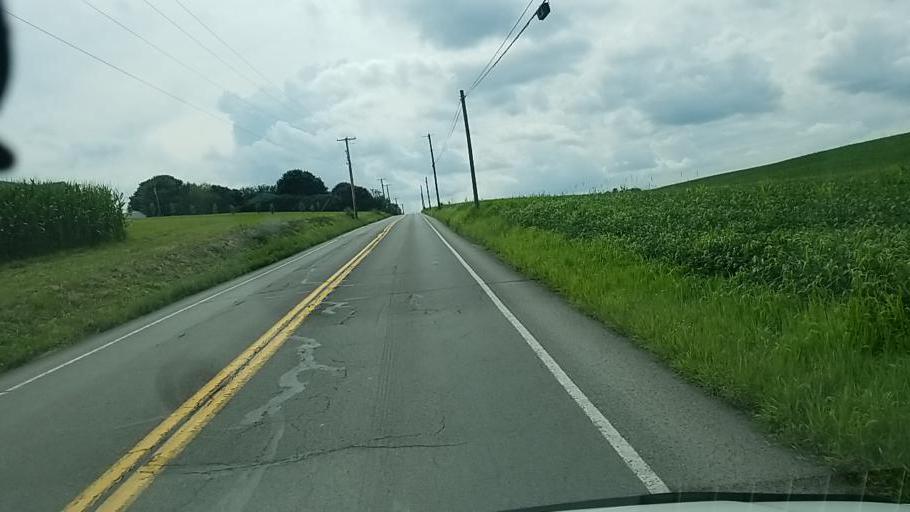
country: US
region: Pennsylvania
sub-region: Dauphin County
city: Elizabethville
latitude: 40.6044
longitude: -76.7986
